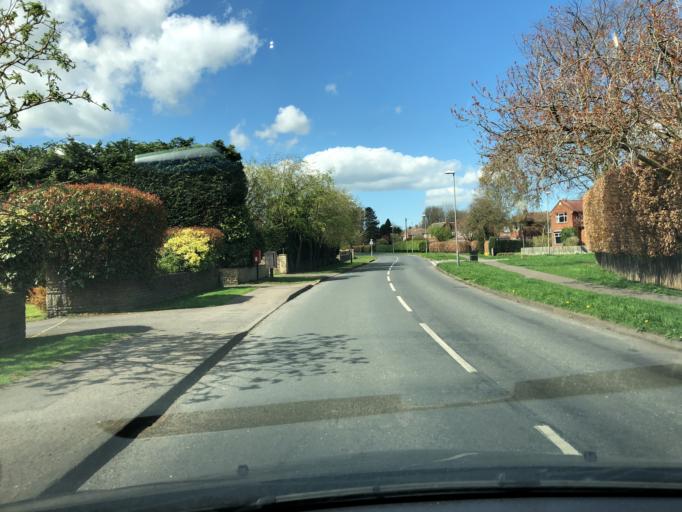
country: GB
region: England
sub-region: North Yorkshire
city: Northallerton
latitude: 54.3317
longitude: -1.4260
